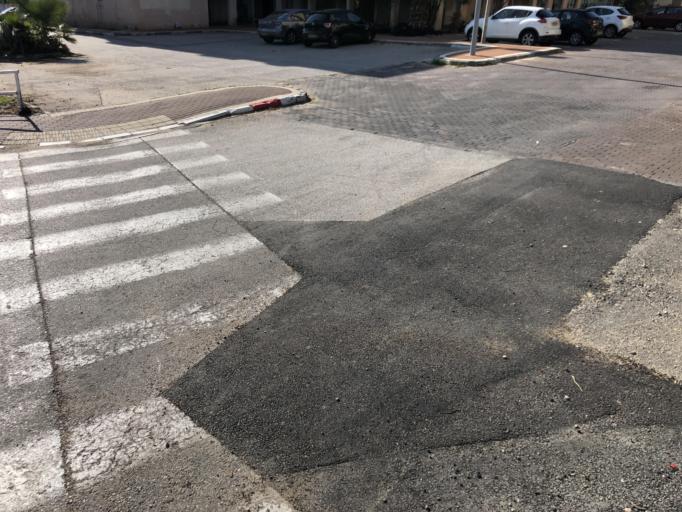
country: IL
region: Northern District
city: `Akko
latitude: 32.9238
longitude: 35.0968
